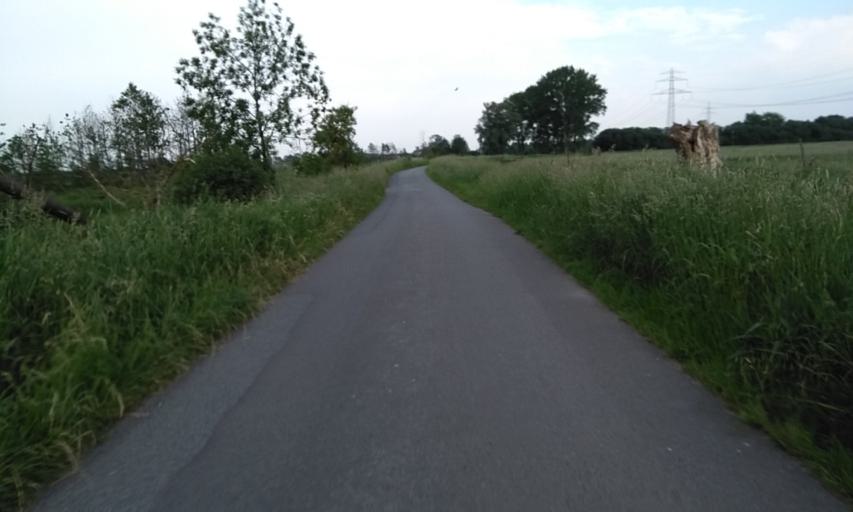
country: DE
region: Lower Saxony
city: Jork
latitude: 53.5031
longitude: 9.6492
